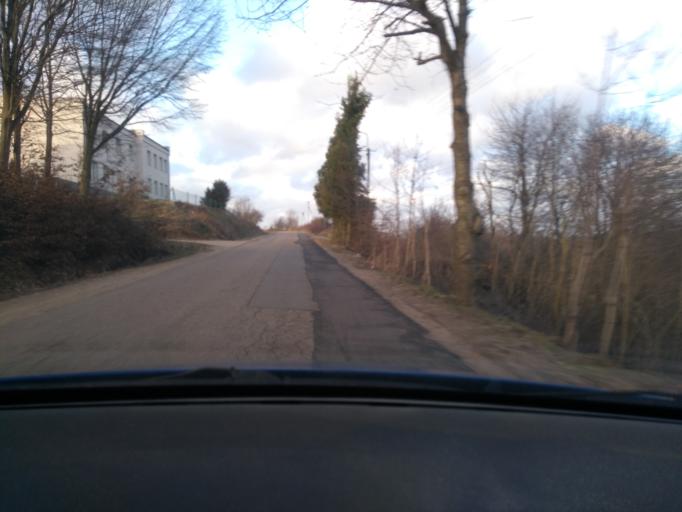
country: PL
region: Pomeranian Voivodeship
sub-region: Powiat kartuski
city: Kartuzy
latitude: 54.3823
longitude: 18.2197
